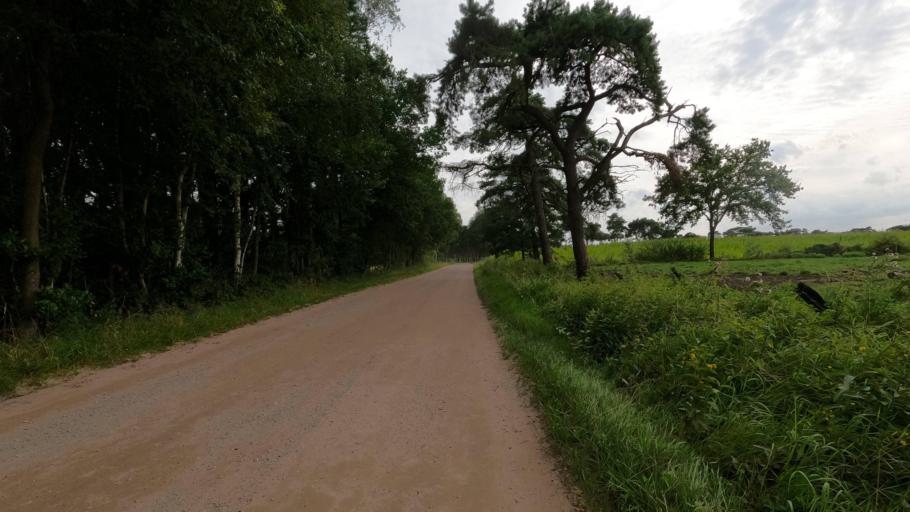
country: BE
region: Flanders
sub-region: Provincie Antwerpen
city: Lille
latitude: 51.2445
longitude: 4.7909
